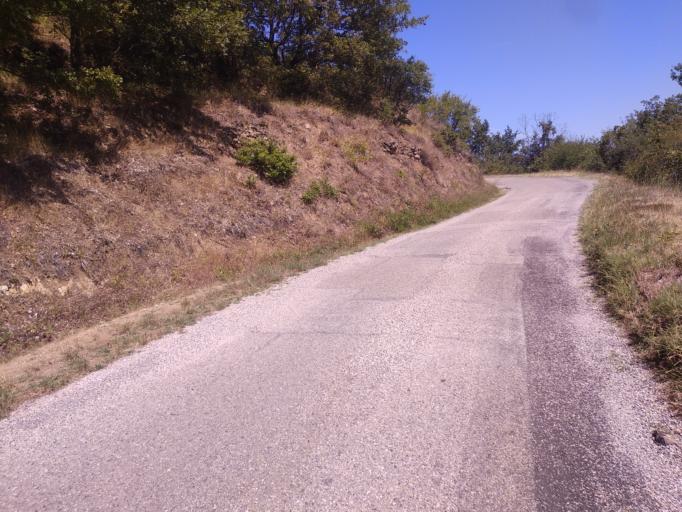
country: FR
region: Rhone-Alpes
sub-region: Departement de l'Ardeche
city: Sarras
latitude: 45.1837
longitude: 4.7907
